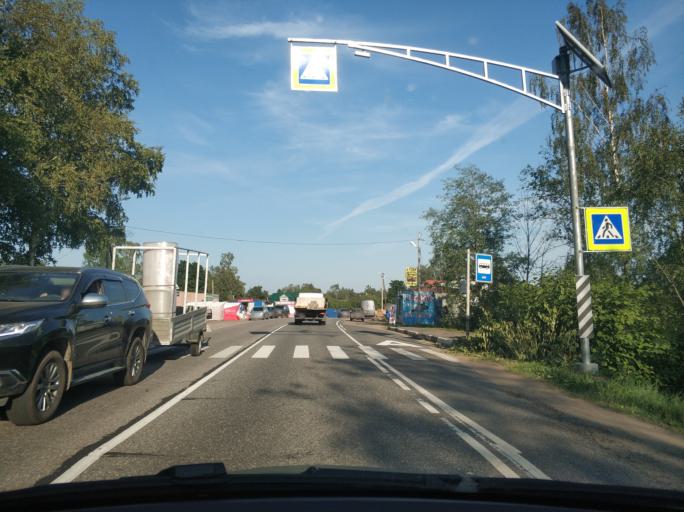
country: RU
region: Leningrad
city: Borisova Griva
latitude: 60.0945
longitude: 30.9738
